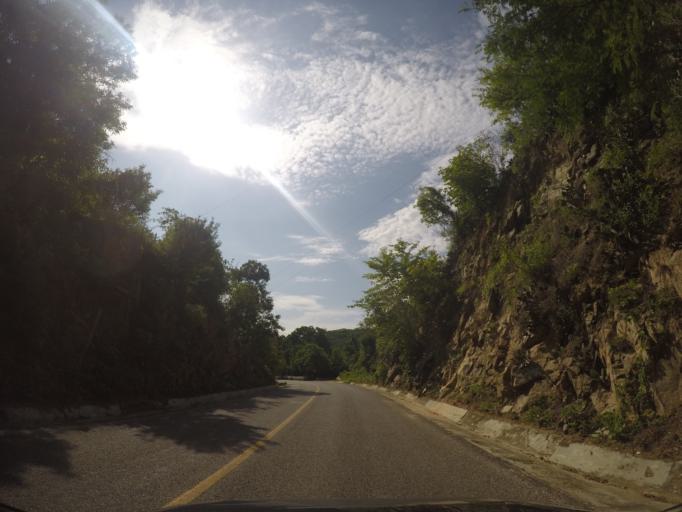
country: MX
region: Oaxaca
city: San Pedro Mixtepec
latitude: 15.9402
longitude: -97.1652
